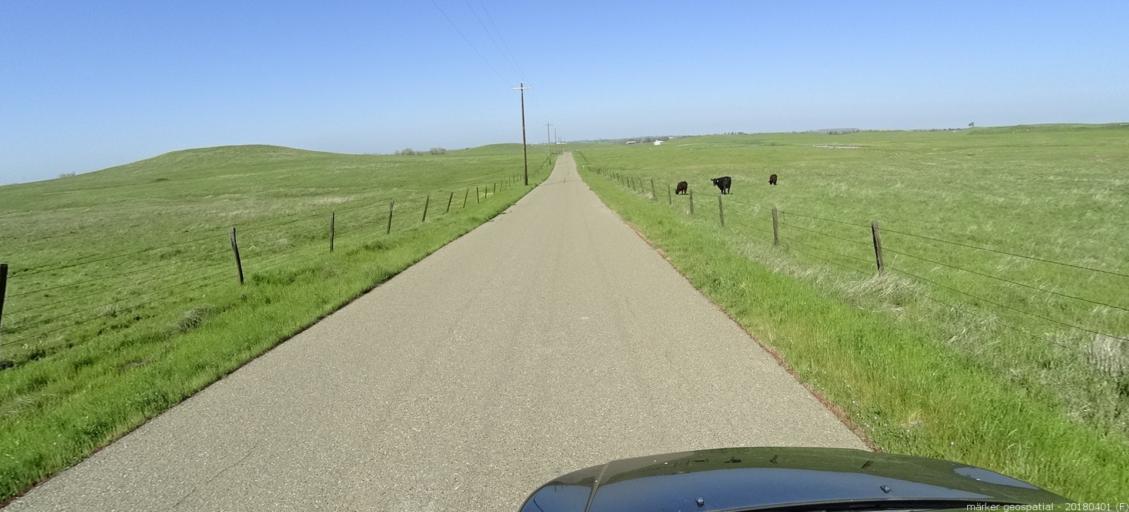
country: US
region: California
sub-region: Sacramento County
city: Rancho Murieta
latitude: 38.4650
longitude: -121.1188
